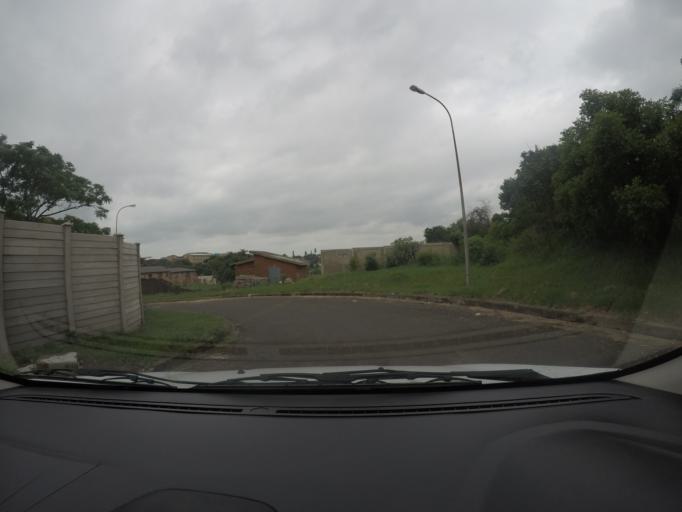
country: ZA
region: KwaZulu-Natal
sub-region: uThungulu District Municipality
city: Empangeni
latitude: -28.7439
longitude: 31.8953
